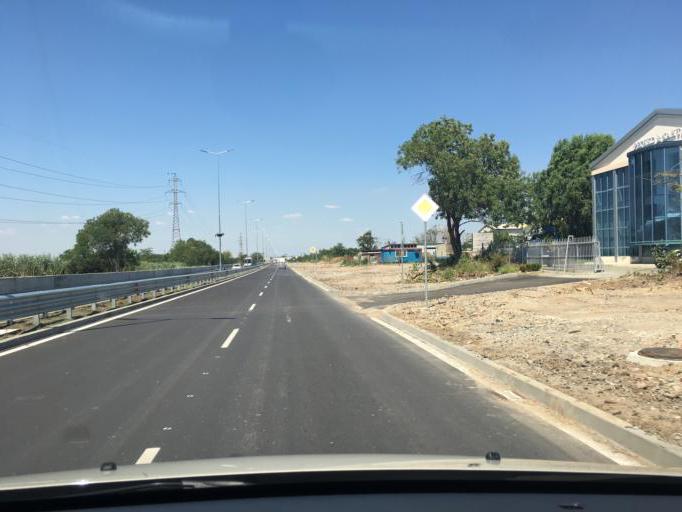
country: BG
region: Burgas
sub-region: Obshtina Burgas
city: Burgas
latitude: 42.5038
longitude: 27.4507
